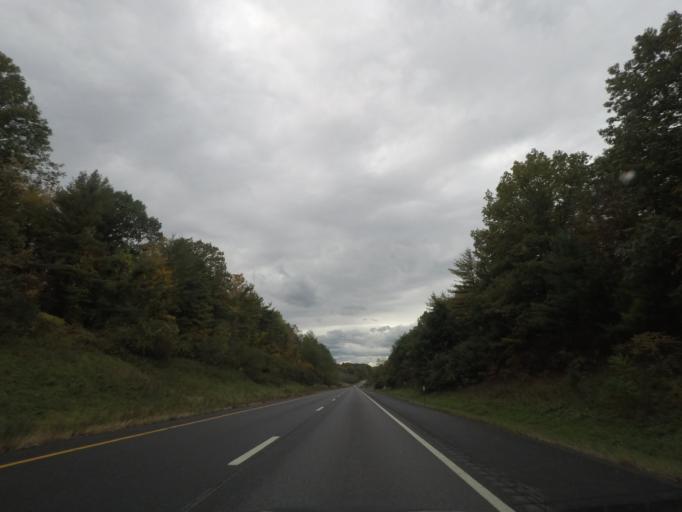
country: US
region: New York
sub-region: Rensselaer County
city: Castleton-on-Hudson
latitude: 42.4962
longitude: -73.7225
